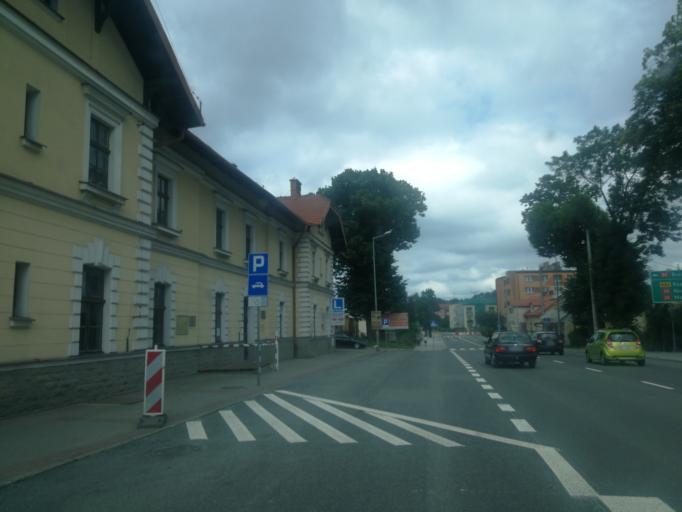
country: PL
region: Subcarpathian Voivodeship
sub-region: Powiat sanocki
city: Sanok
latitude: 49.5532
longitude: 22.2115
